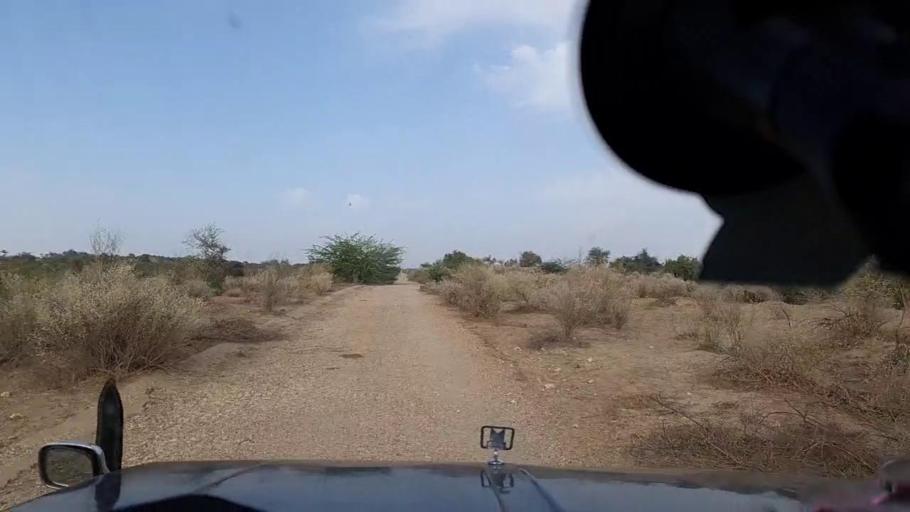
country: PK
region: Sindh
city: Diplo
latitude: 24.5394
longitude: 69.4653
